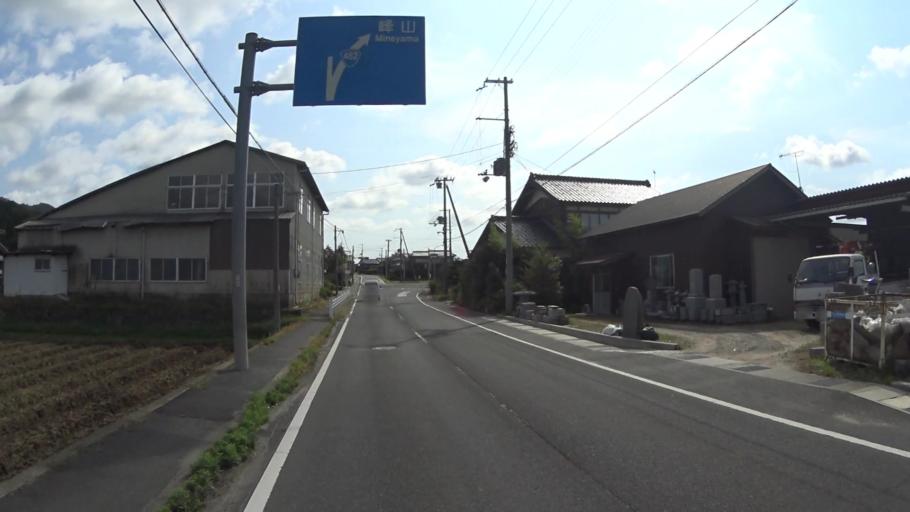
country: JP
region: Kyoto
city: Miyazu
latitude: 35.6511
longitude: 135.0920
